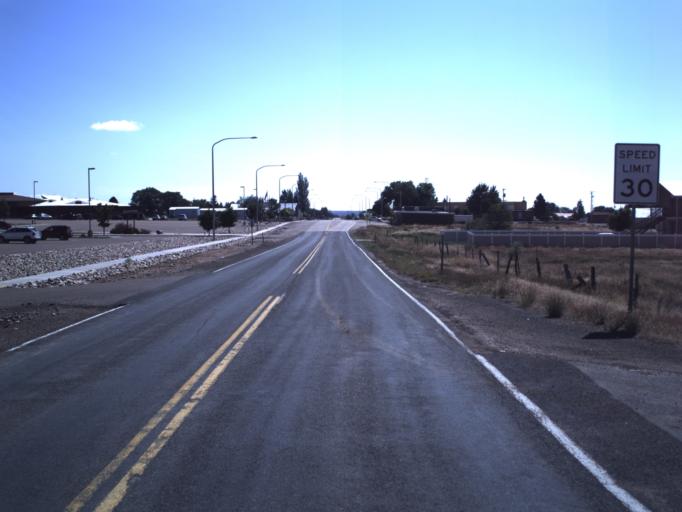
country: US
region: Utah
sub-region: Duchesne County
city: Duchesne
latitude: 40.3592
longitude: -110.2926
